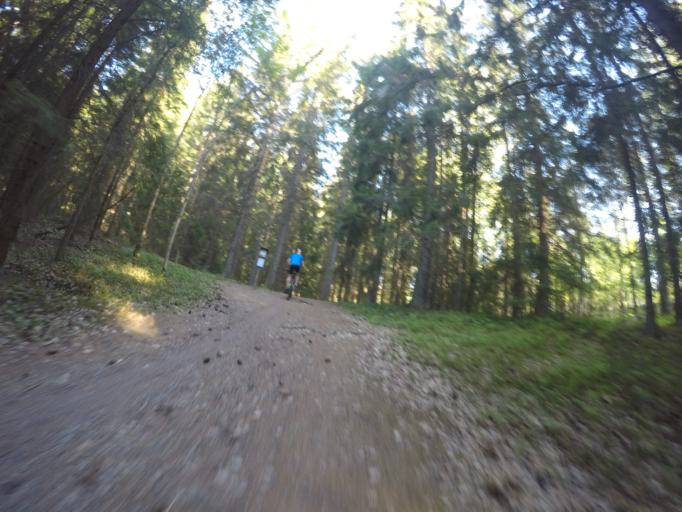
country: SE
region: Soedermanland
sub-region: Eskilstuna Kommun
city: Eskilstuna
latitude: 59.3519
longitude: 16.5197
